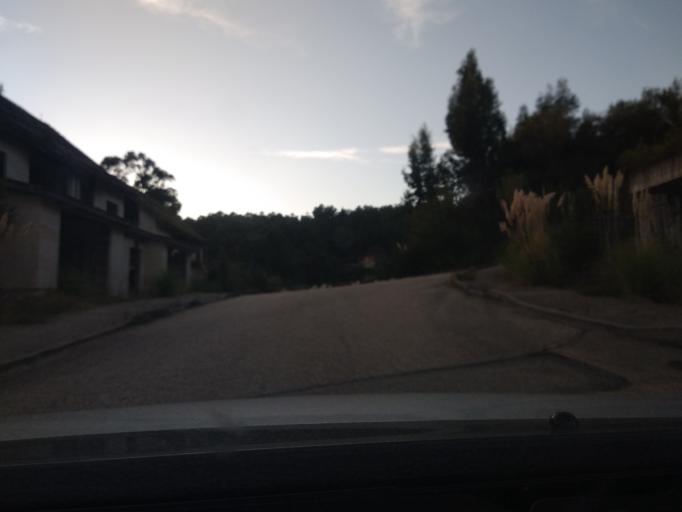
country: ES
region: Galicia
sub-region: Provincia de Pontevedra
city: Moana
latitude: 42.2971
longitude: -8.6902
